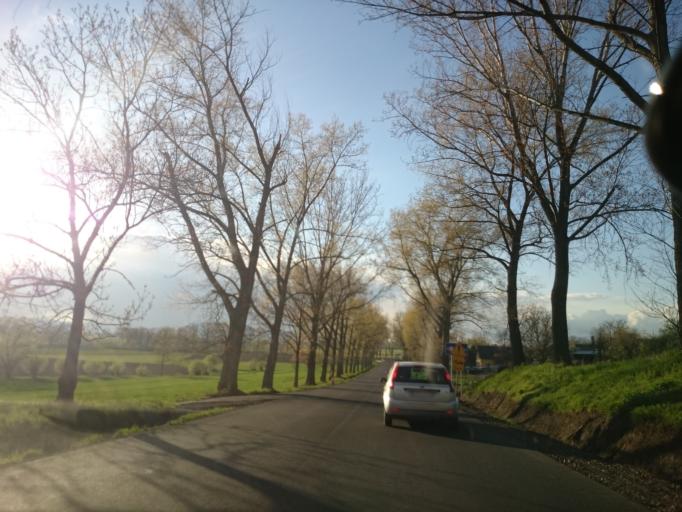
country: PL
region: Lower Silesian Voivodeship
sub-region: Powiat zabkowicki
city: Kamieniec Zabkowicki
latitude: 50.5599
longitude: 16.8497
